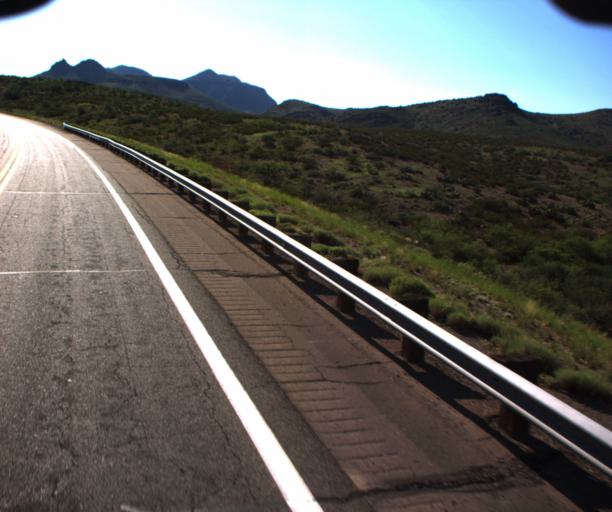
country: US
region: Arizona
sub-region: Greenlee County
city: Clifton
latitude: 32.8472
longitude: -109.3935
